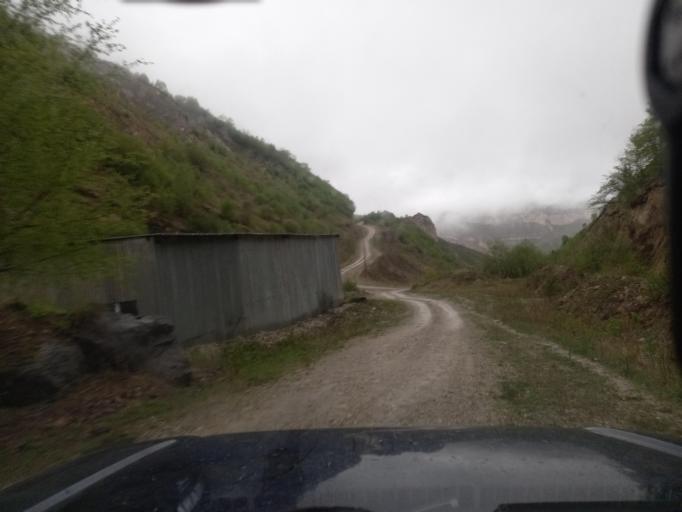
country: RU
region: Kabardino-Balkariya
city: Zhankhoteko
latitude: 43.4976
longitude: 43.1542
